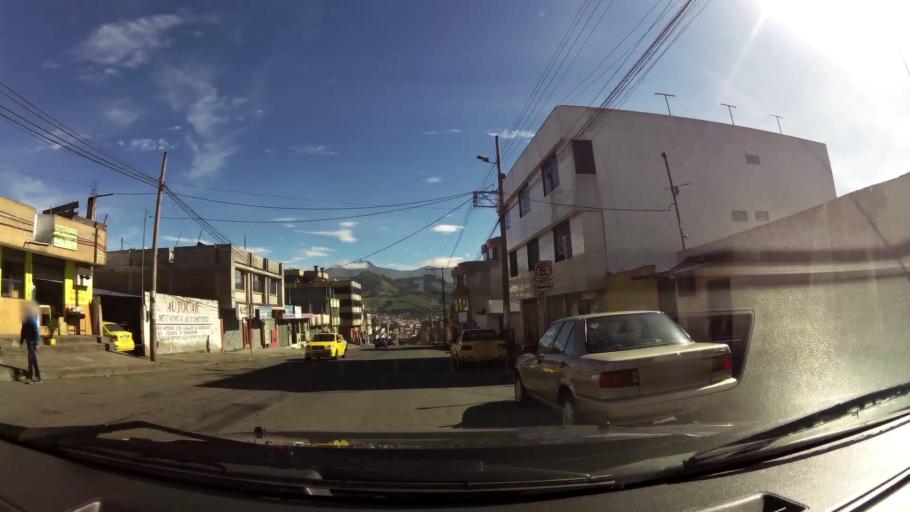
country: EC
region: Pichincha
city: Quito
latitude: -0.3071
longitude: -78.5665
